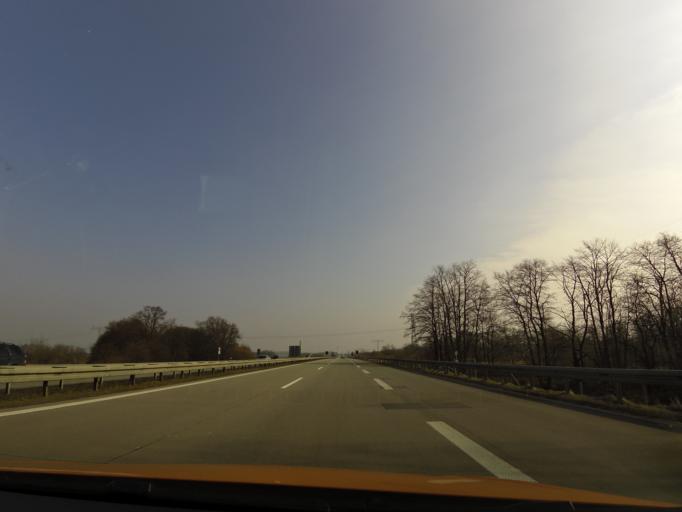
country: DE
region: Brandenburg
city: Frankfurt (Oder)
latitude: 52.3204
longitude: 14.4793
